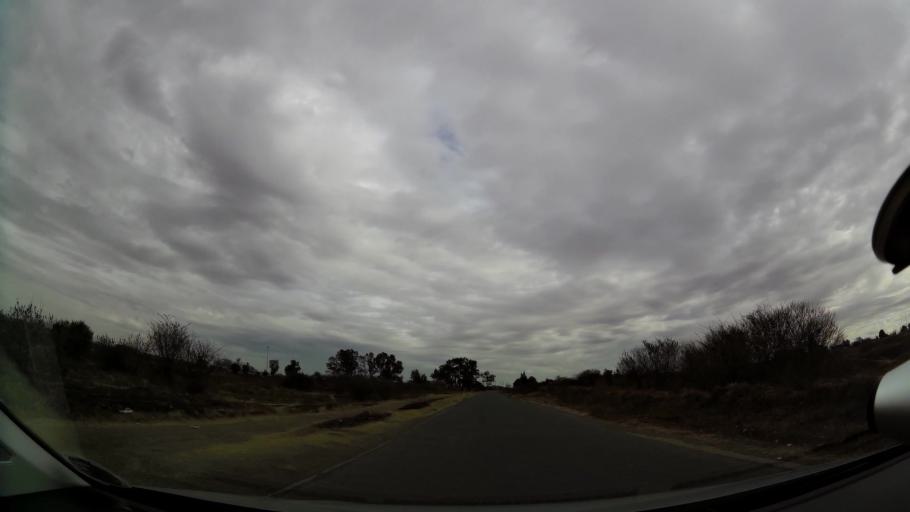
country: ZA
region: Orange Free State
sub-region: Fezile Dabi District Municipality
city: Kroonstad
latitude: -27.6508
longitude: 27.2141
